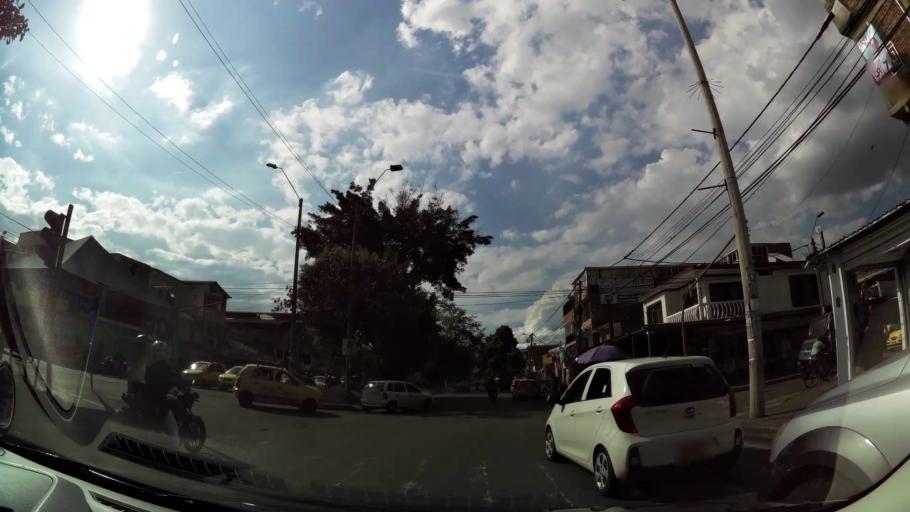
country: CO
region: Valle del Cauca
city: Cali
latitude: 3.4172
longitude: -76.5059
